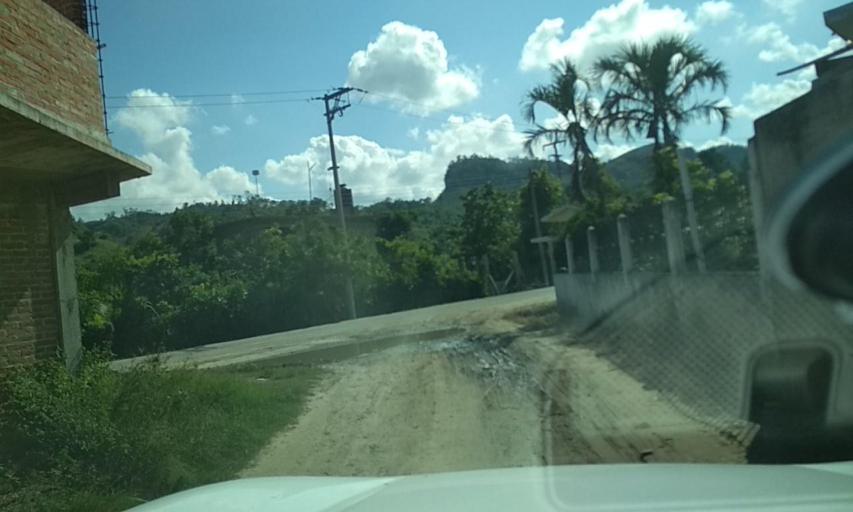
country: MX
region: Veracruz
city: Cazones de Herrera
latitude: 20.6417
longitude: -97.3086
